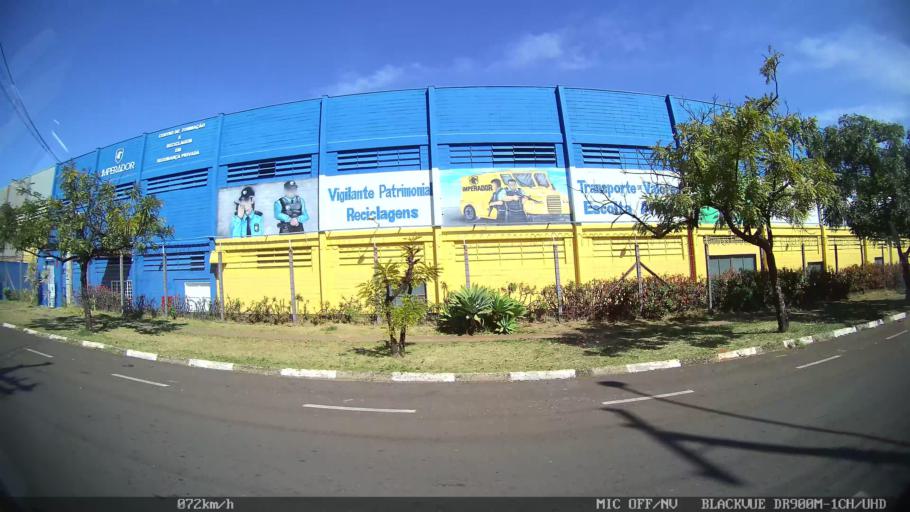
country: BR
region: Sao Paulo
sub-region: Franca
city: Franca
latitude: -20.5473
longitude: -47.4551
